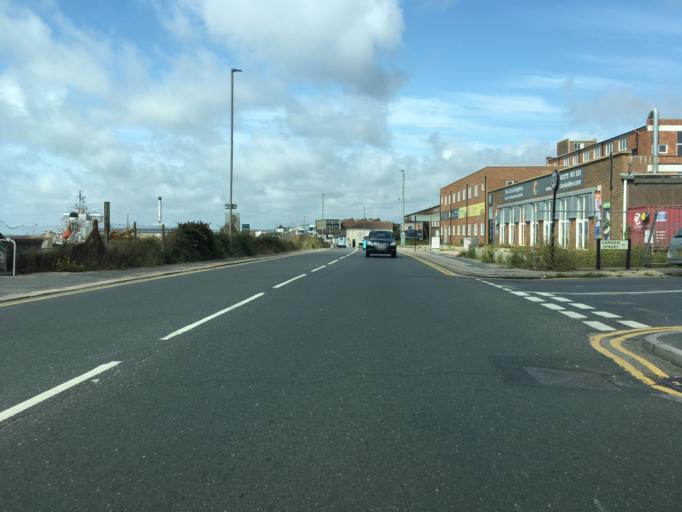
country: GB
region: England
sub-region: East Sussex
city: Portslade
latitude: 50.8299
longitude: -0.2103
